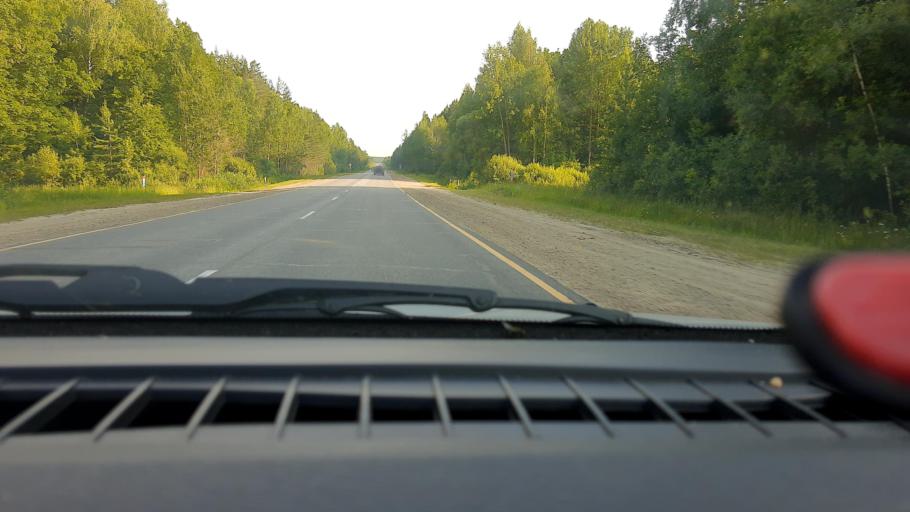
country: RU
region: Nizjnij Novgorod
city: Arzamas
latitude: 55.4108
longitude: 43.9149
